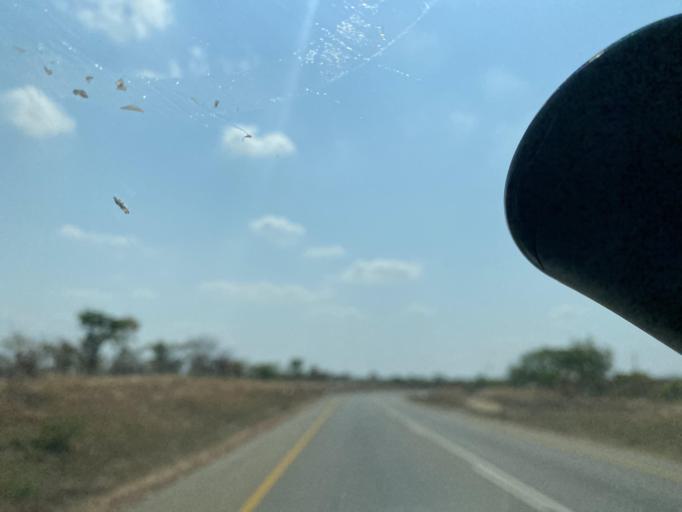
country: ZM
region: Lusaka
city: Chongwe
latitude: -15.5352
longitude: 28.6433
